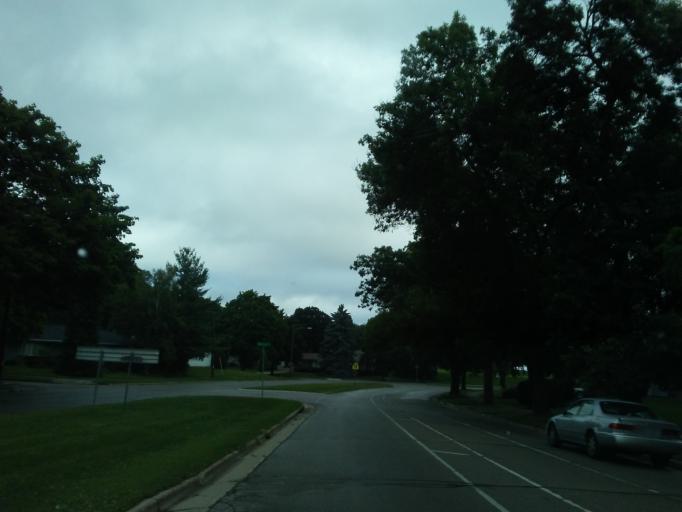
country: US
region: Wisconsin
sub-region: Dane County
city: Shorewood Hills
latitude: 43.0619
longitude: -89.4578
